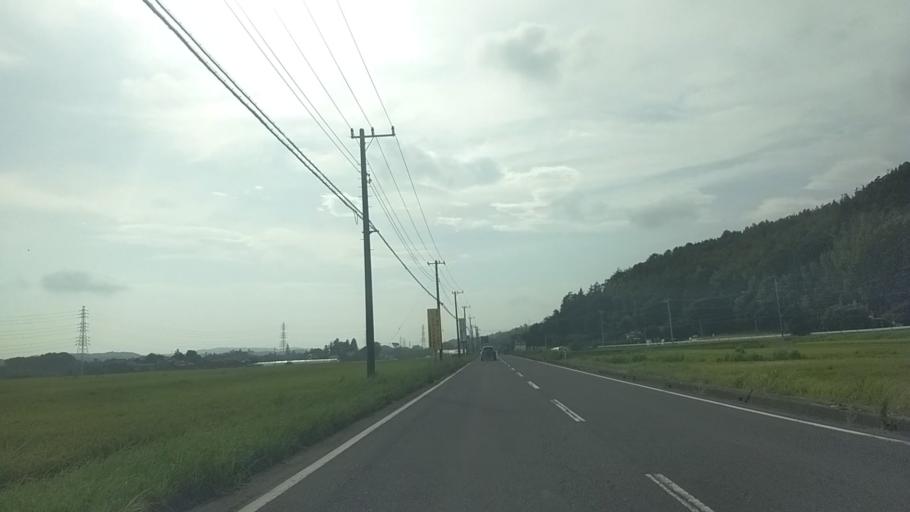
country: JP
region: Chiba
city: Kisarazu
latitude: 35.3095
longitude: 139.9732
